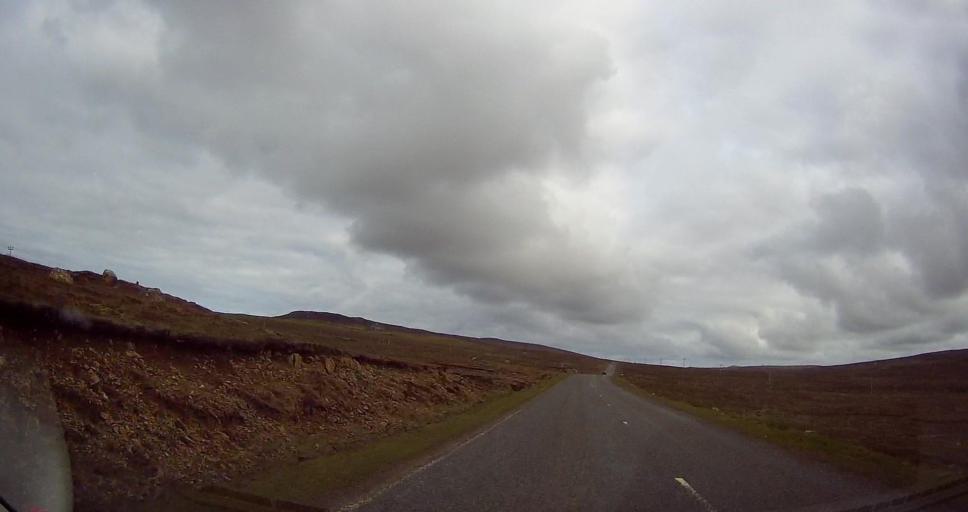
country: GB
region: Scotland
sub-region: Shetland Islands
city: Shetland
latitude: 60.7029
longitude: -0.9202
